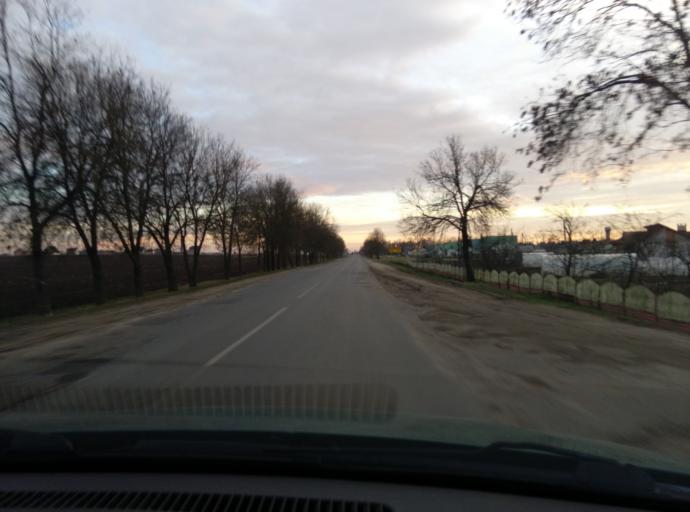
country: BY
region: Minsk
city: Horad Barysaw
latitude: 54.2794
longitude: 28.4947
